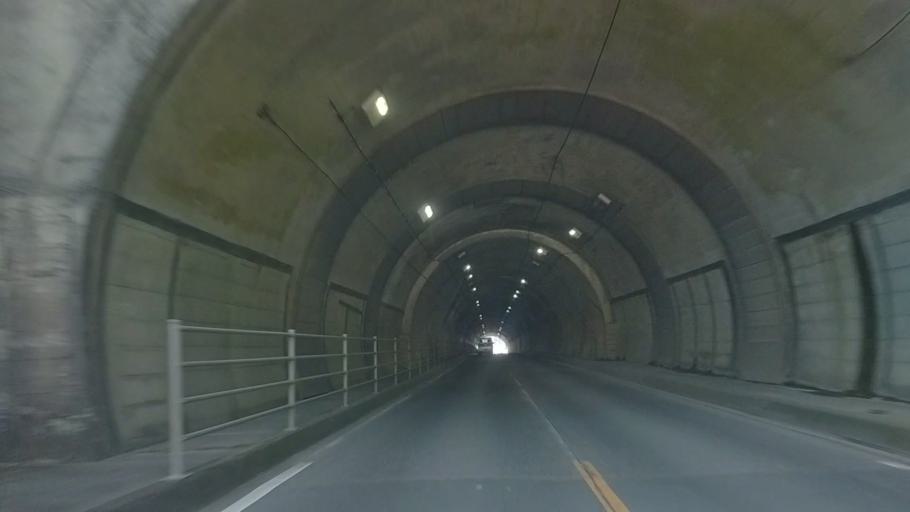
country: JP
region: Shizuoka
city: Fujinomiya
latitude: 35.3684
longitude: 138.4472
